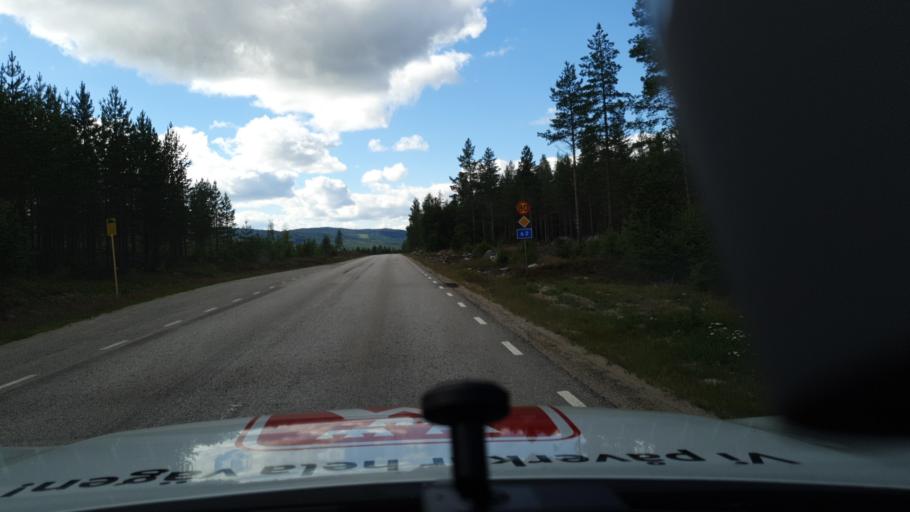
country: NO
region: Hedmark
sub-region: Trysil
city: Innbygda
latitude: 61.0216
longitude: 12.5086
